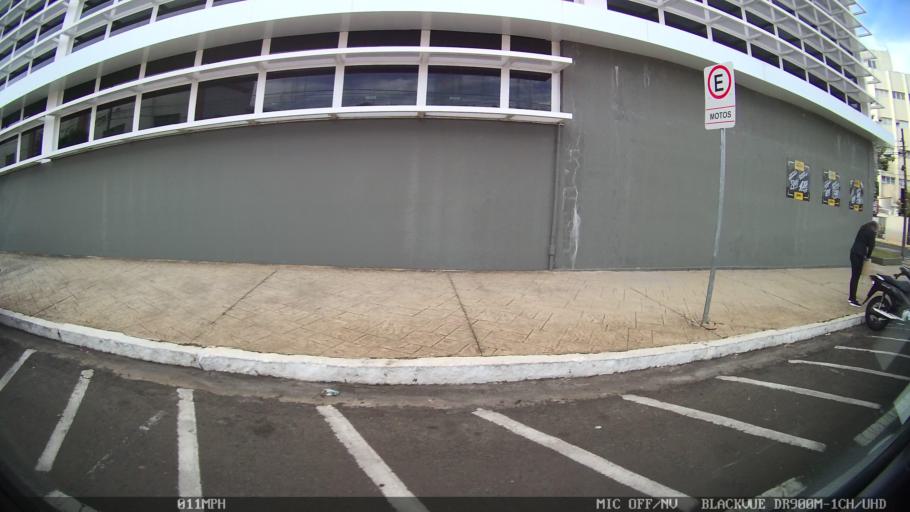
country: BR
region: Sao Paulo
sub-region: Catanduva
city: Catanduva
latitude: -21.1312
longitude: -48.9715
